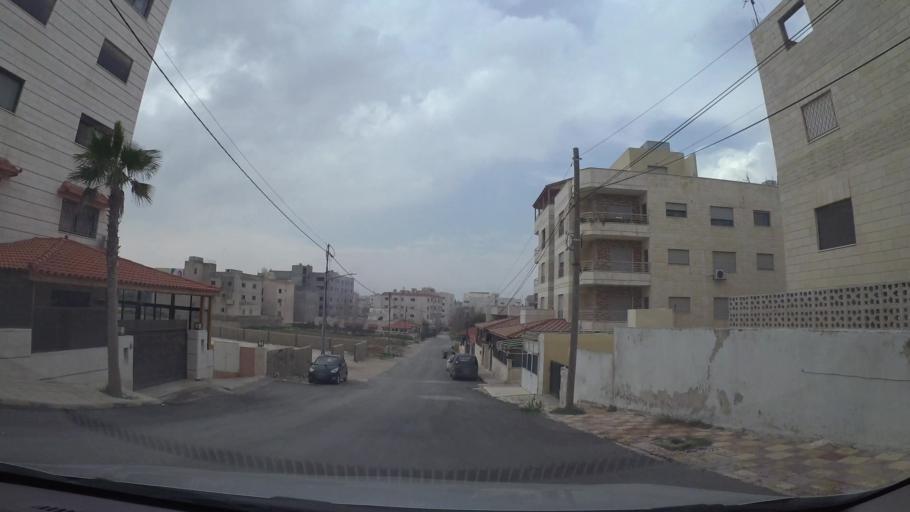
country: JO
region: Amman
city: Umm as Summaq
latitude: 31.8892
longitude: 35.8513
